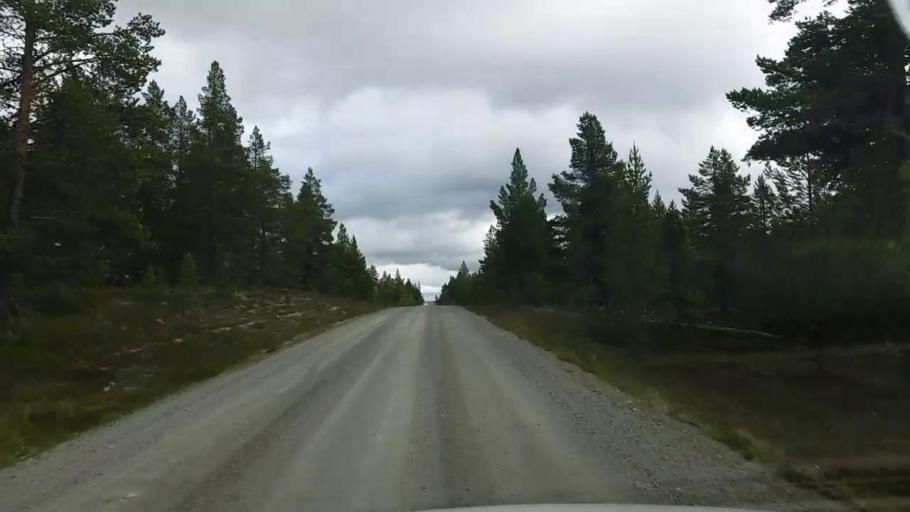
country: NO
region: Hedmark
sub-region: Engerdal
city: Engerdal
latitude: 62.3375
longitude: 12.6229
